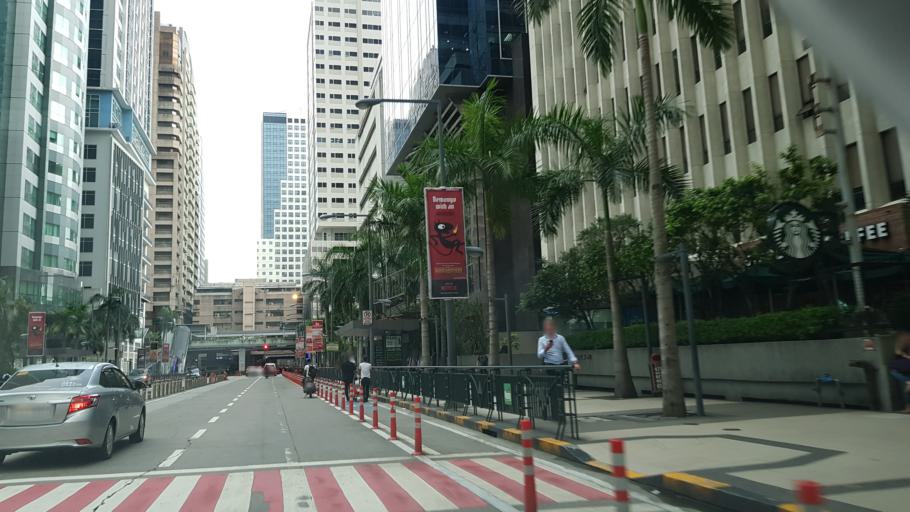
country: PH
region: Metro Manila
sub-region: Pasig
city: Pasig City
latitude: 14.5859
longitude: 121.0623
